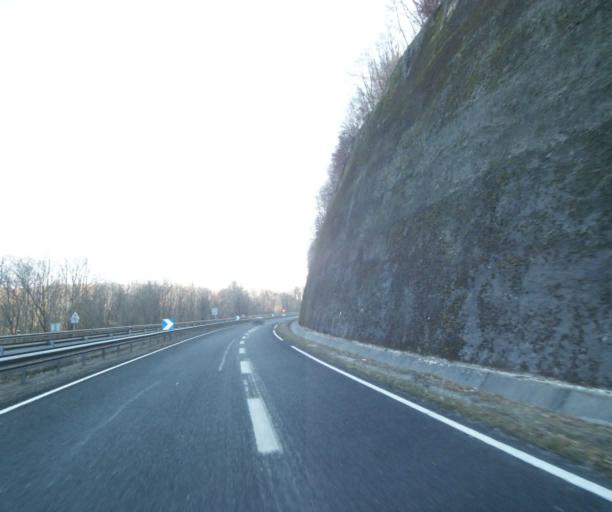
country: FR
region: Champagne-Ardenne
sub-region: Departement de la Haute-Marne
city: Chevillon
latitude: 48.5405
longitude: 5.0973
